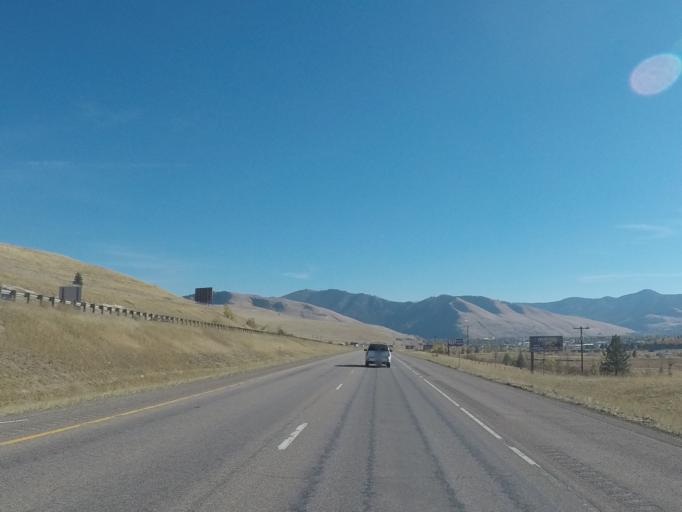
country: US
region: Montana
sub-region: Missoula County
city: Missoula
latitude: 46.9068
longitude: -114.0255
